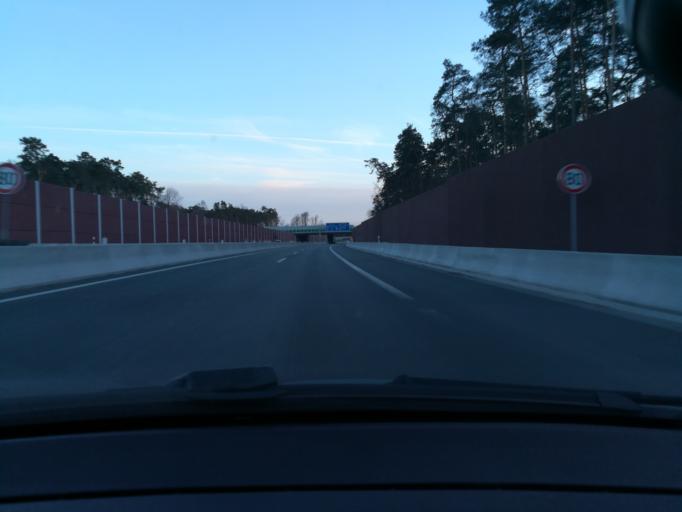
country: DE
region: North Rhine-Westphalia
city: Halle
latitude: 52.0514
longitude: 8.3404
